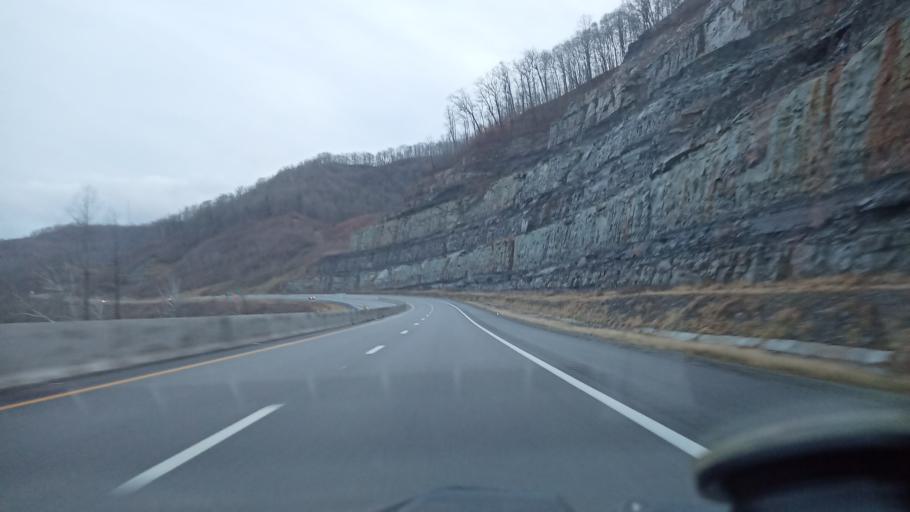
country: US
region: West Virginia
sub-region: Logan County
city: Logan
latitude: 37.8156
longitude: -81.9378
